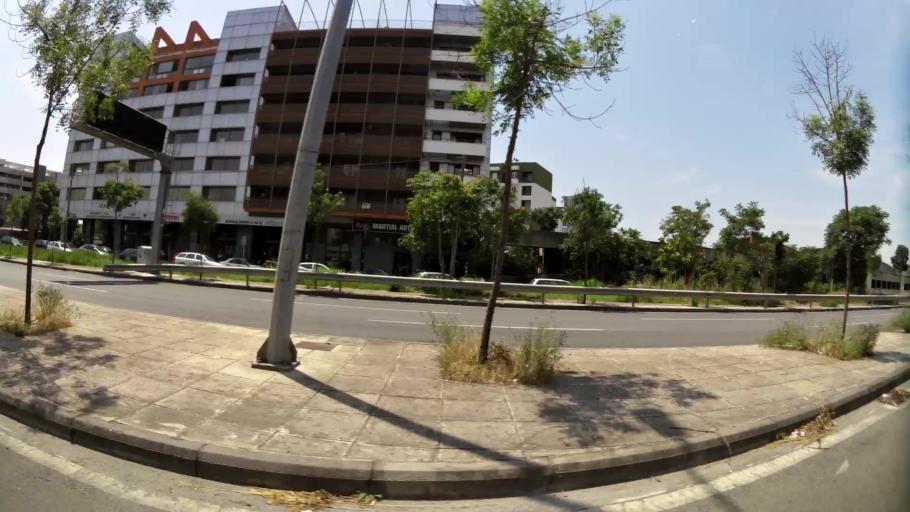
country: GR
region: Central Macedonia
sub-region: Nomos Thessalonikis
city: Ampelokipoi
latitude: 40.6467
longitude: 22.9162
